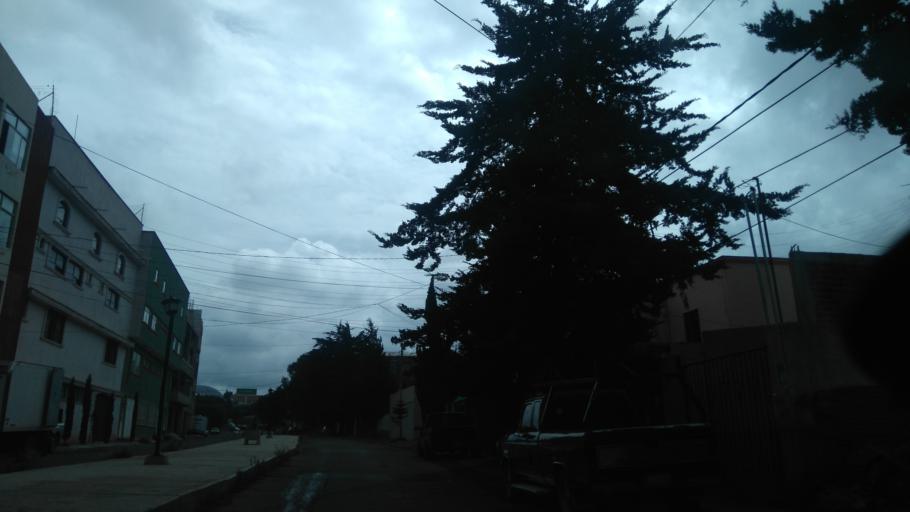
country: MX
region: Zacatecas
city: Zacatecas
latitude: 22.7567
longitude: -102.5893
